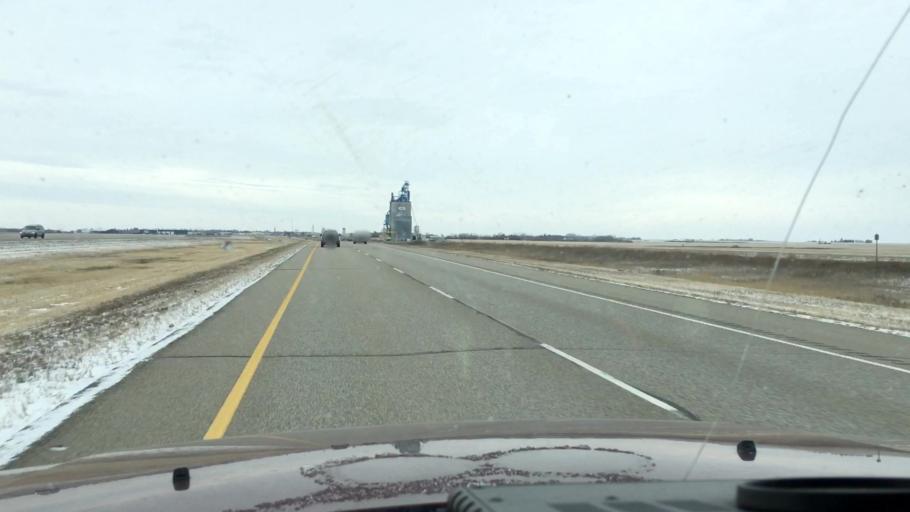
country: CA
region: Saskatchewan
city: Watrous
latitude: 51.2865
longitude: -106.0240
